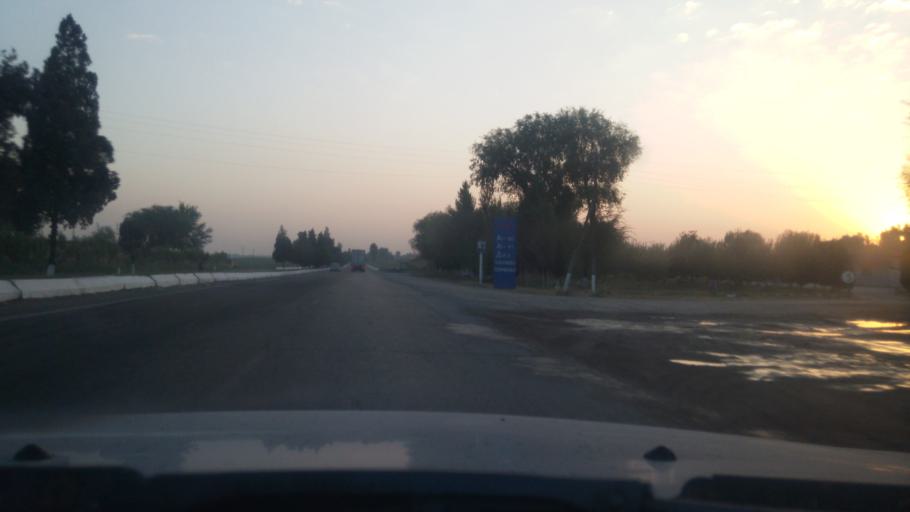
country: UZ
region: Toshkent
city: Zafar
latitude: 41.0410
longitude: 68.8818
